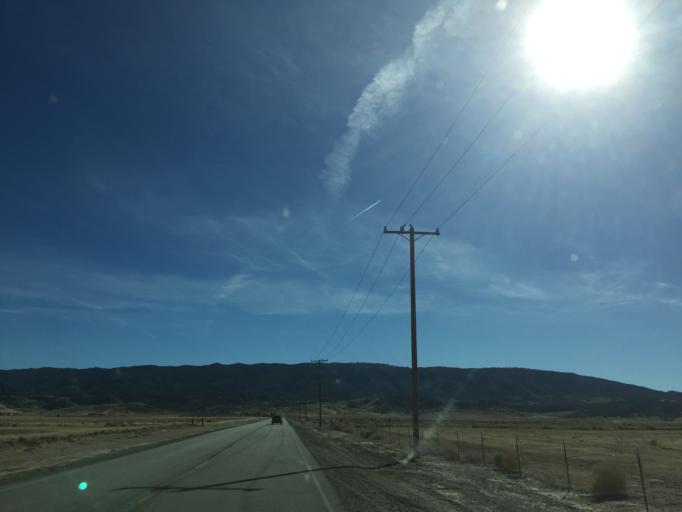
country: US
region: California
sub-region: Kern County
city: Lebec
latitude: 34.7975
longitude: -118.6611
